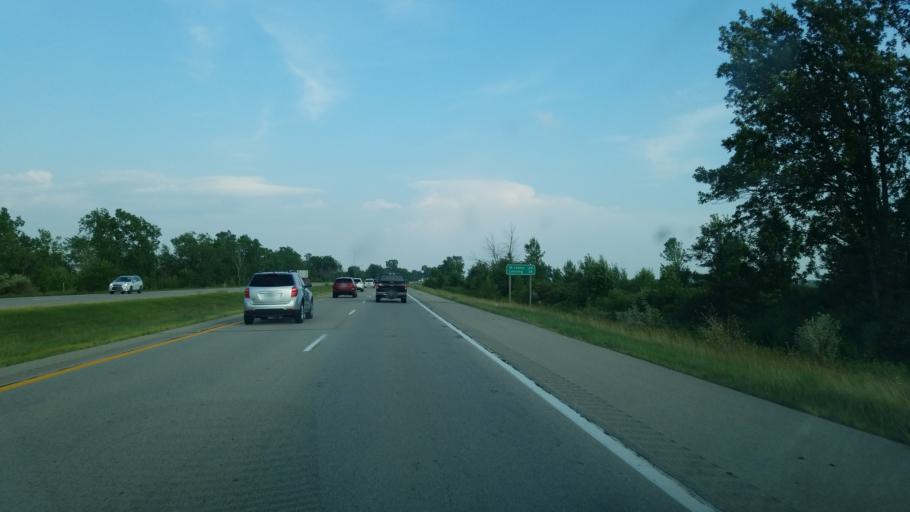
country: US
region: Michigan
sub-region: Gratiot County
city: Ithaca
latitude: 43.2802
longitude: -84.5765
